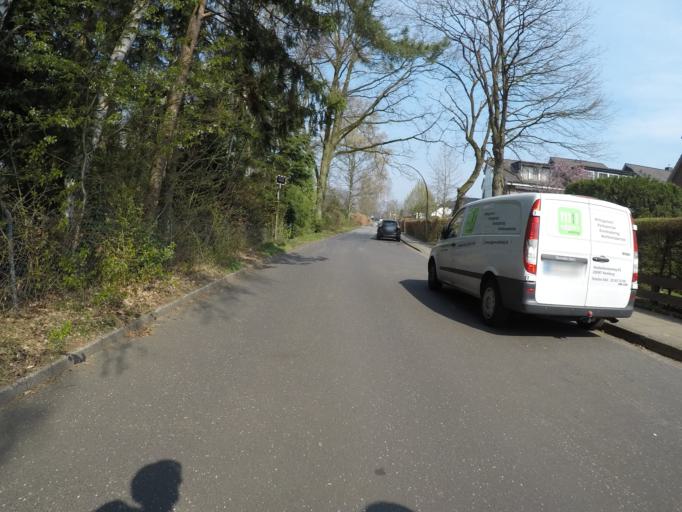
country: DE
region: Hamburg
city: Sasel
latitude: 53.6629
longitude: 10.1014
